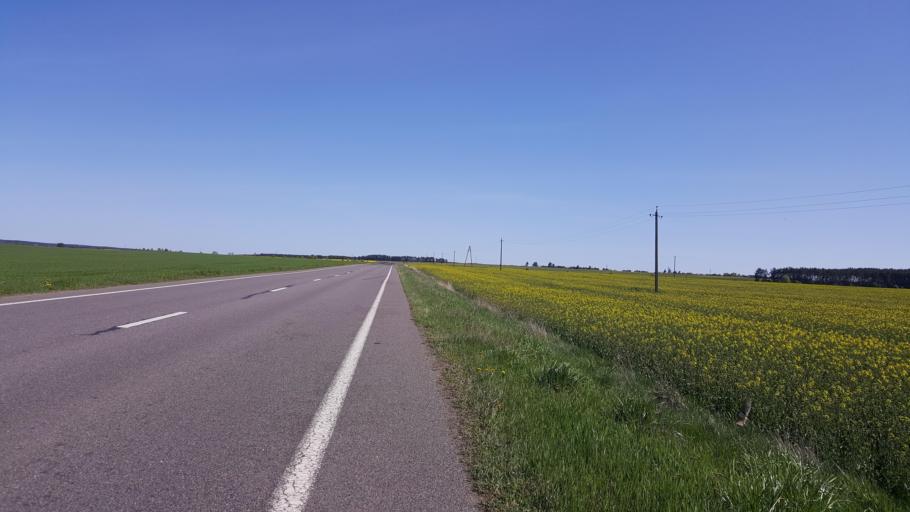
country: BY
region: Brest
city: Kamyanyets
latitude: 52.4186
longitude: 23.8450
